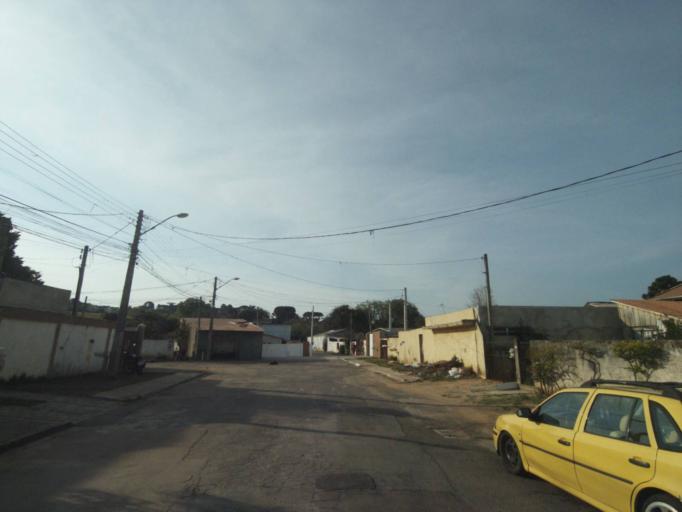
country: BR
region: Parana
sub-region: Curitiba
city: Curitiba
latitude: -25.4564
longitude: -49.3141
